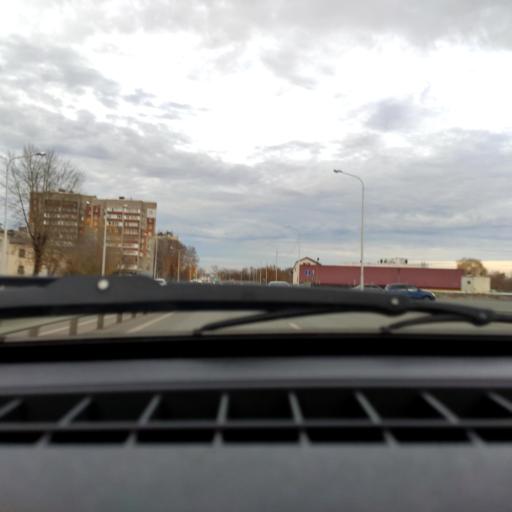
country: RU
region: Bashkortostan
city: Ufa
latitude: 54.8002
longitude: 56.1316
